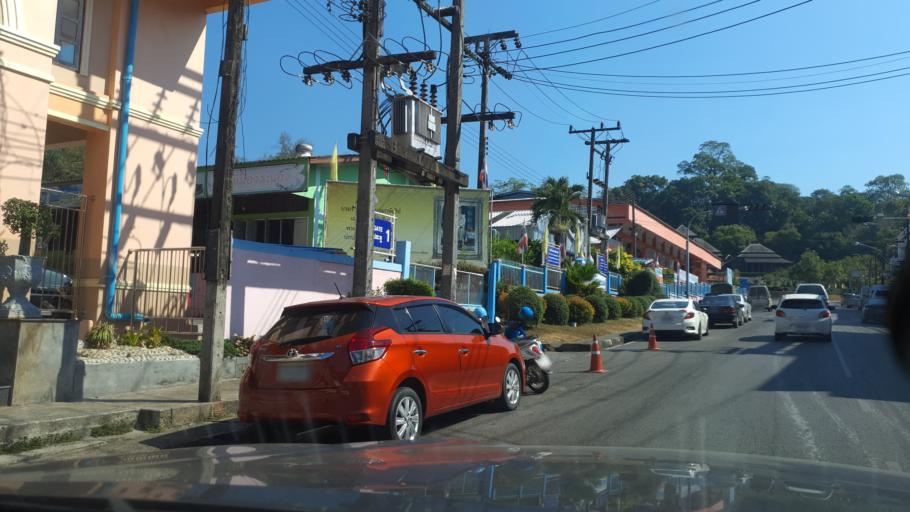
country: TH
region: Ranong
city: Ranong
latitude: 9.9644
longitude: 98.6347
